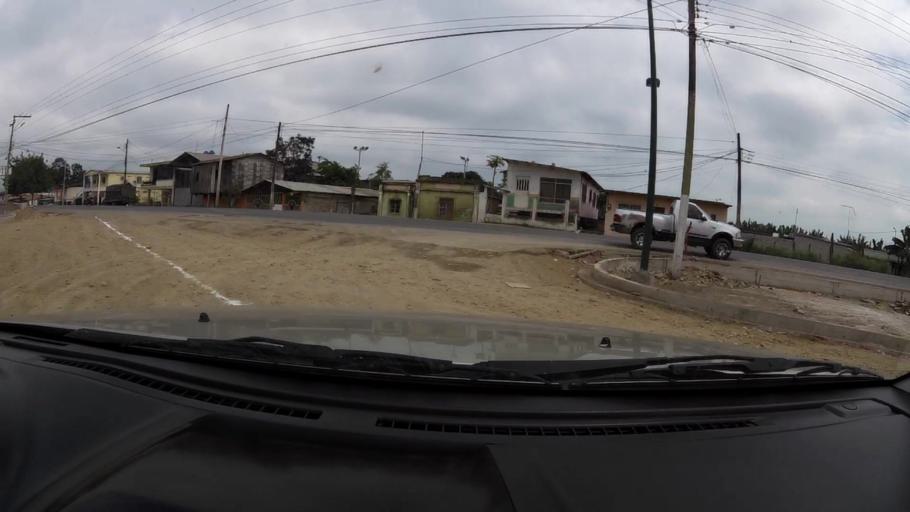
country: EC
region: El Oro
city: Pasaje
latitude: -3.2474
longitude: -79.8295
